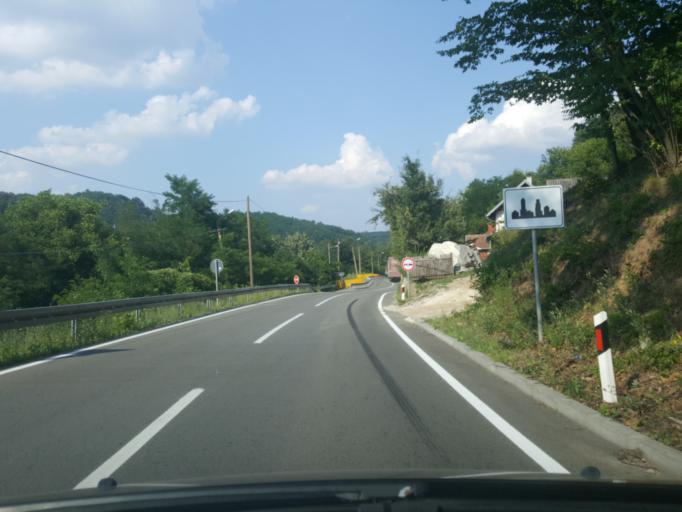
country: RS
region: Central Serbia
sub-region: Sumadijski Okrug
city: Arangelovac
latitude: 44.1831
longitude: 20.5409
